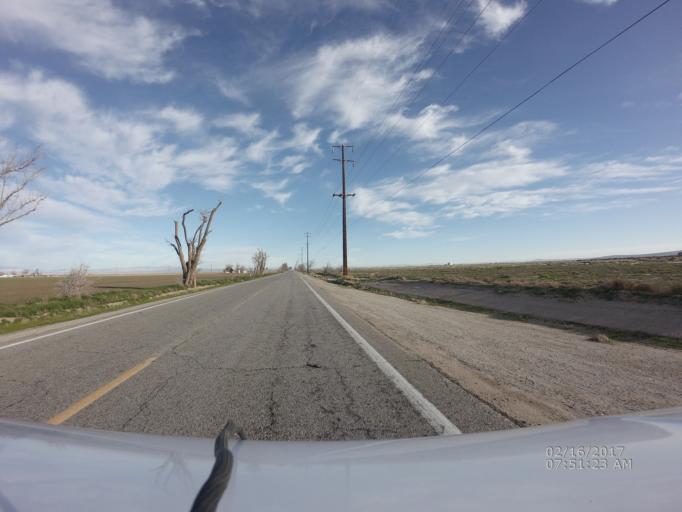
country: US
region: California
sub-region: Los Angeles County
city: Lancaster
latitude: 34.7207
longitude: -117.9698
